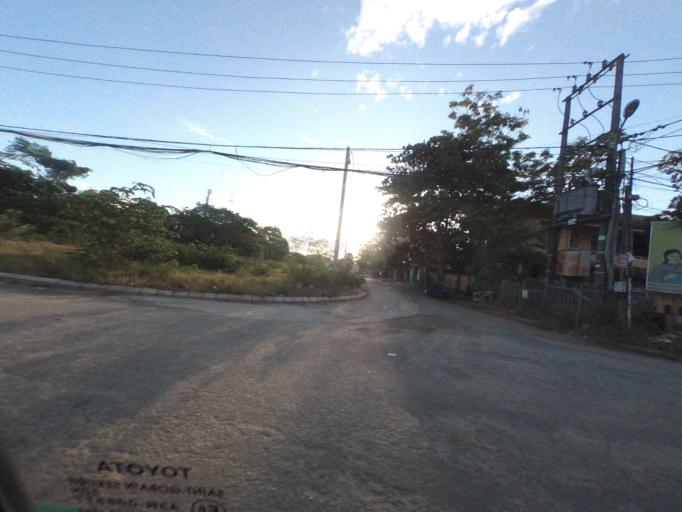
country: VN
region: Thua Thien-Hue
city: Hue
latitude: 16.4931
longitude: 107.5837
